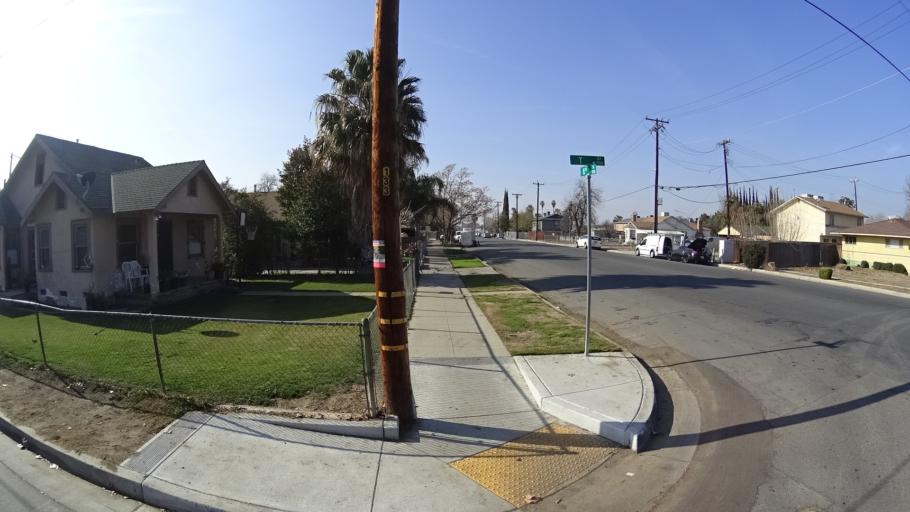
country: US
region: California
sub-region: Kern County
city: Bakersfield
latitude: 35.3645
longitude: -119.0073
